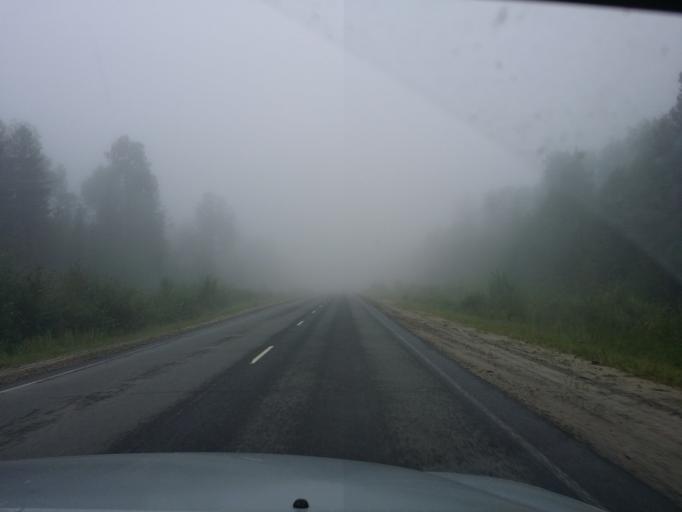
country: RU
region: Khanty-Mansiyskiy Avtonomnyy Okrug
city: Gornopravdinsk
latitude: 59.6685
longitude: 70.0069
